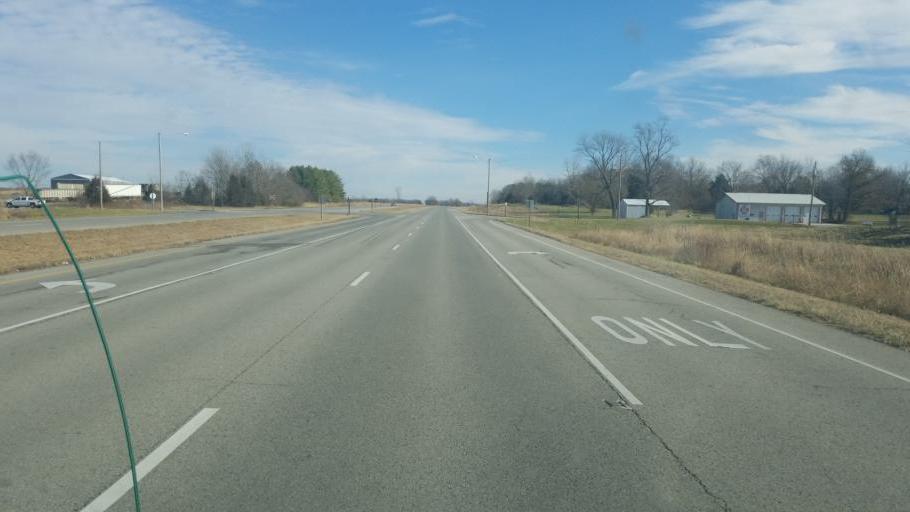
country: US
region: Illinois
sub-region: Williamson County
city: Marion
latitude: 37.7326
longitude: -88.8004
